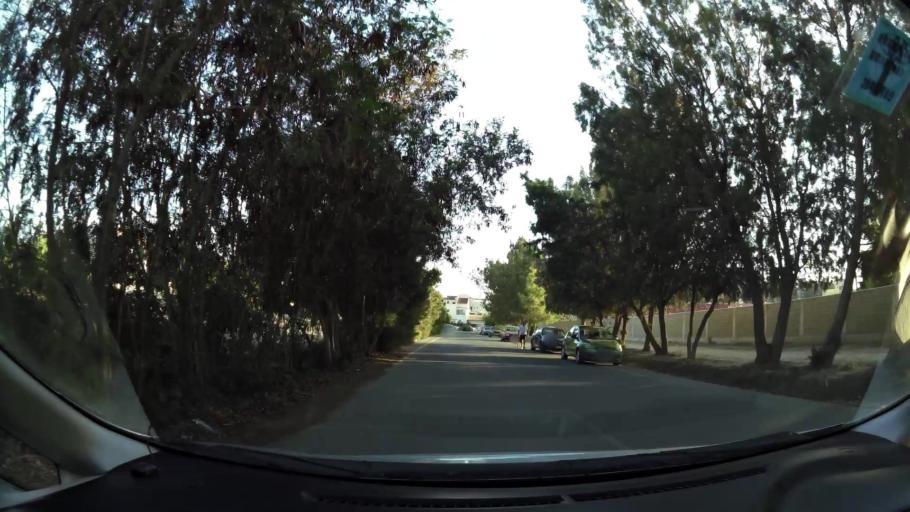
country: CY
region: Larnaka
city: Larnaca
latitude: 34.9234
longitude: 33.6067
